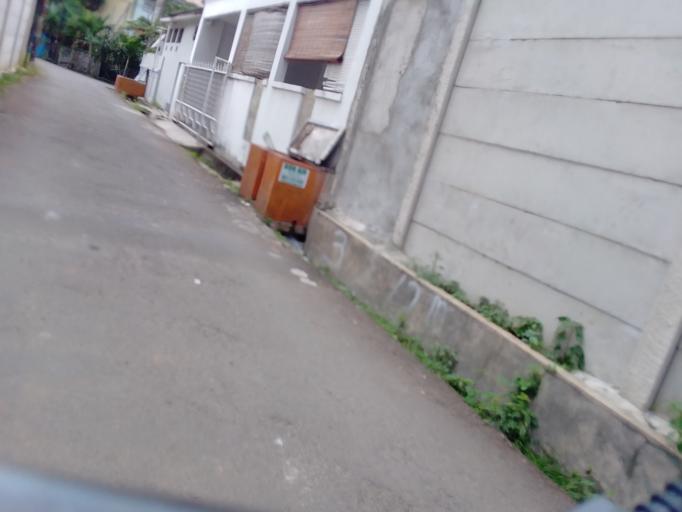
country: ID
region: Jakarta Raya
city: Jakarta
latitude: -6.2161
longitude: 106.8111
